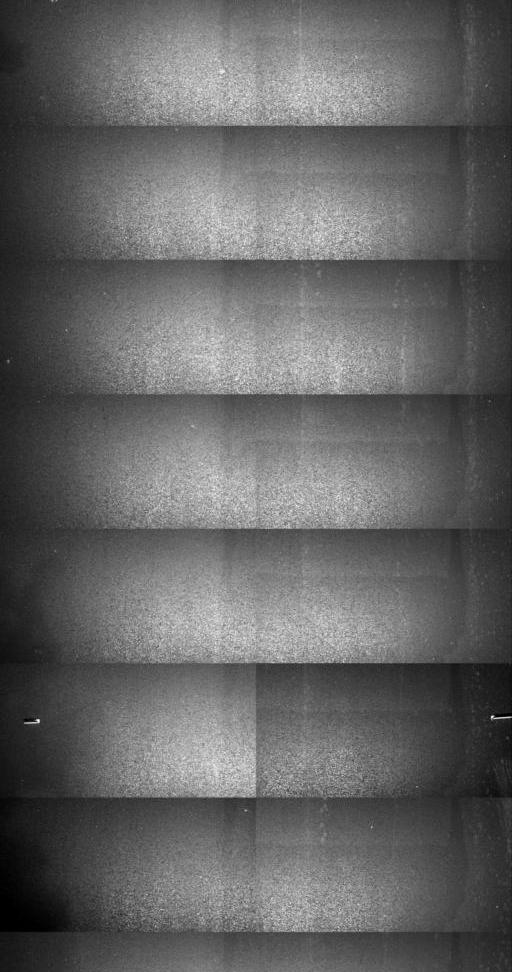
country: US
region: Vermont
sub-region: Franklin County
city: Richford
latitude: 44.9807
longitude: -72.5311
